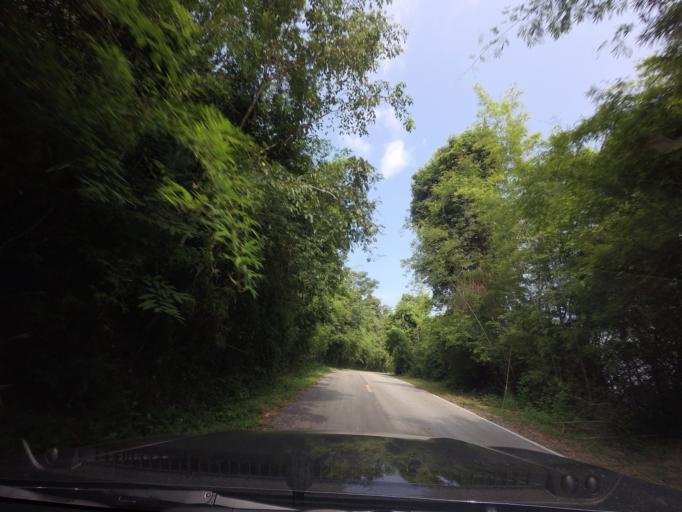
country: TH
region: Loei
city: Chiang Khan
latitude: 17.8180
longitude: 101.5563
